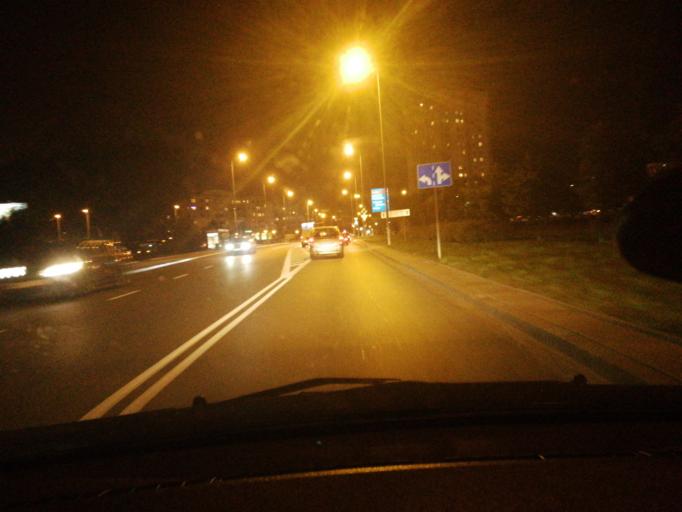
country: PL
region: Masovian Voivodeship
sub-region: Warszawa
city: Targowek
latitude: 52.2936
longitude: 21.0526
